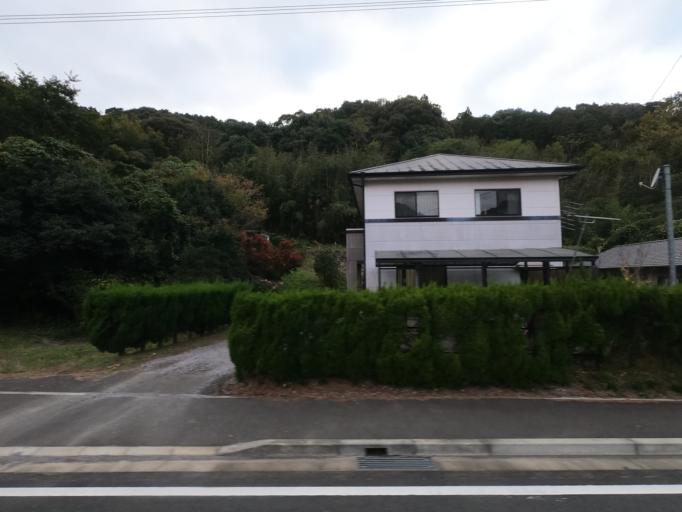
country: JP
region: Kumamoto
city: Minamata
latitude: 32.2586
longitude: 130.5101
